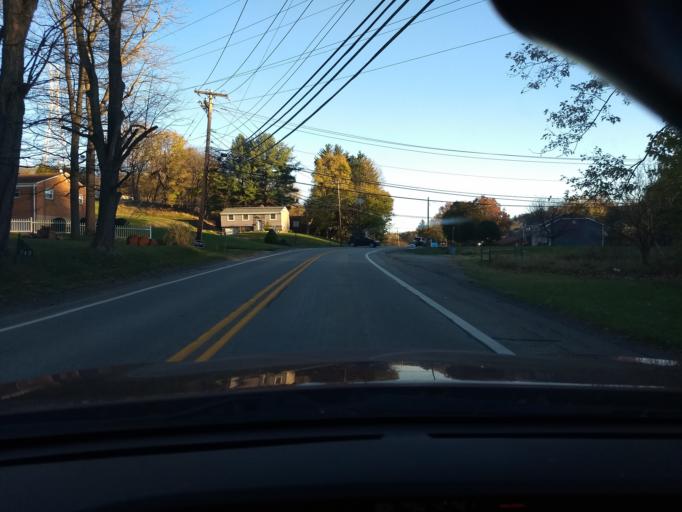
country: US
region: Pennsylvania
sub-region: Allegheny County
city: Bethel Park
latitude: 40.3047
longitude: -80.0575
